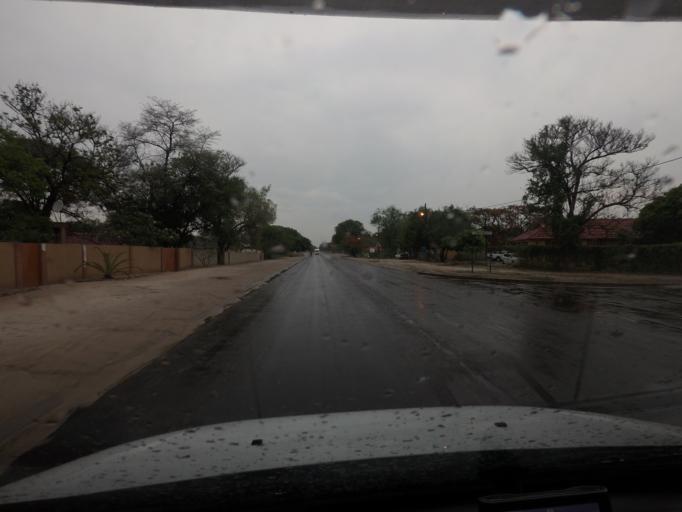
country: ZM
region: Western
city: Sesheke
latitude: -17.4896
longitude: 24.2846
